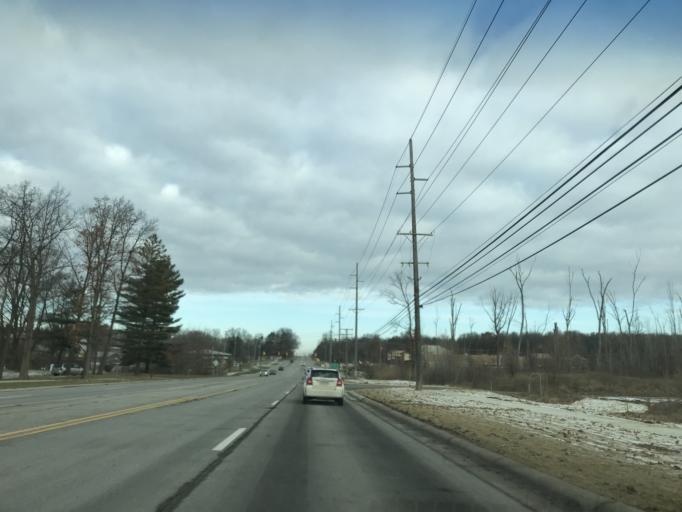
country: US
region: Michigan
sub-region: Oakland County
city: Clarkston
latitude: 42.7493
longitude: -83.3801
